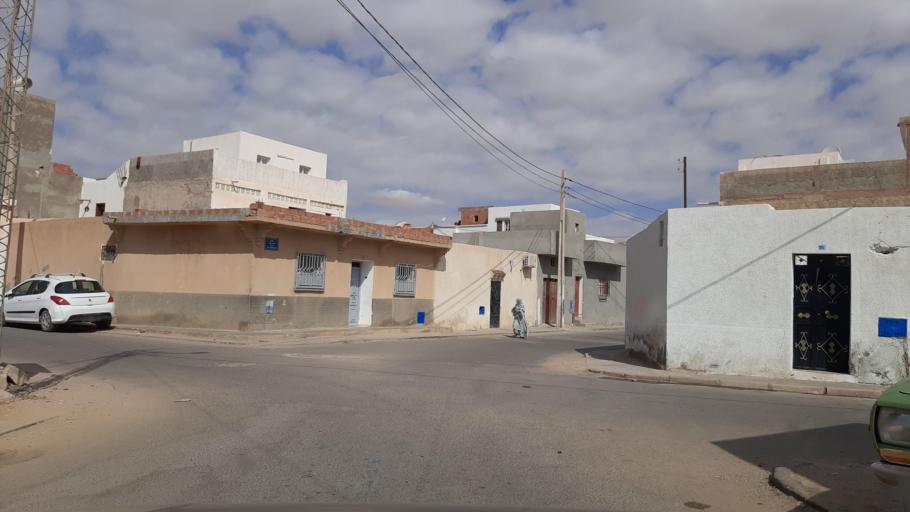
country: TN
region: Tataouine
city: Tataouine
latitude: 32.9293
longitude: 10.4533
